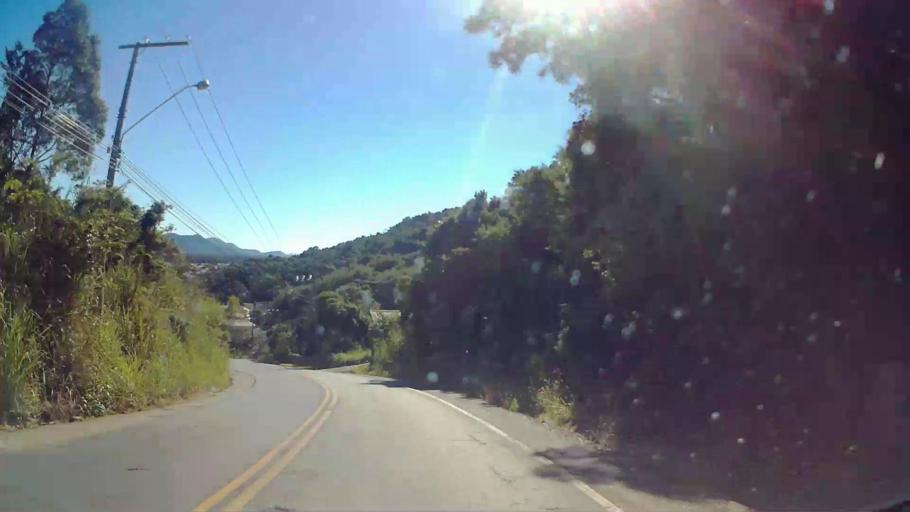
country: BR
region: Santa Catarina
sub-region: Florianopolis
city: Lagoa
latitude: -27.5948
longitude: -48.4361
